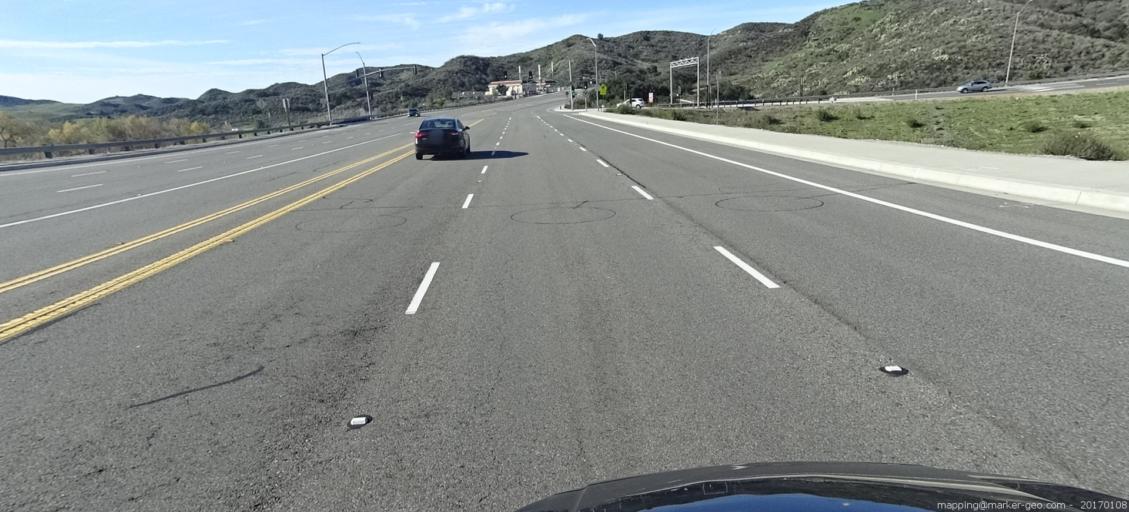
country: US
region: California
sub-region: Orange County
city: Las Flores
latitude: 33.5875
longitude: -117.6099
